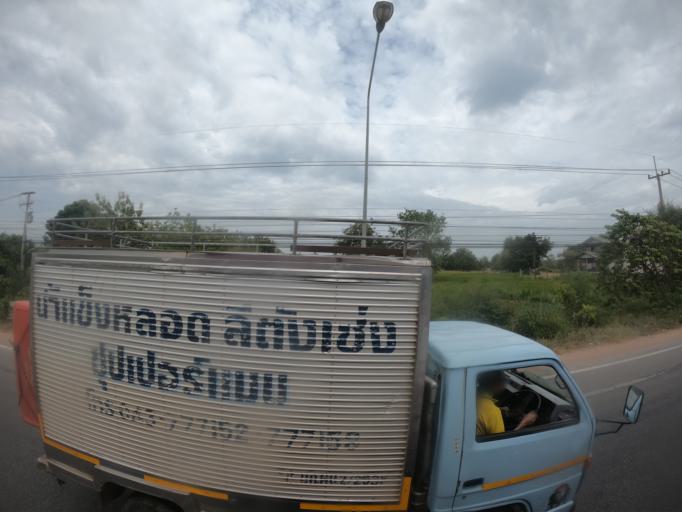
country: TH
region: Maha Sarakham
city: Maha Sarakham
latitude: 16.1640
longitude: 103.3399
